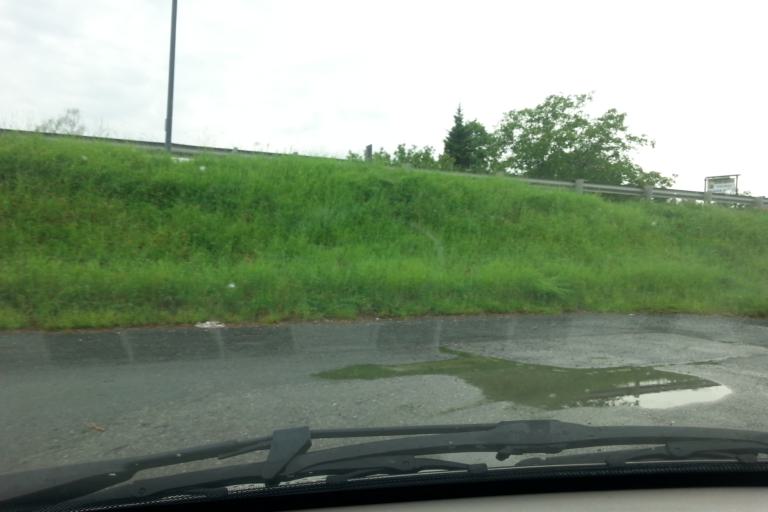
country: IT
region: Piedmont
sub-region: Provincia di Torino
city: Alpignano
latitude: 45.1029
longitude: 7.5103
